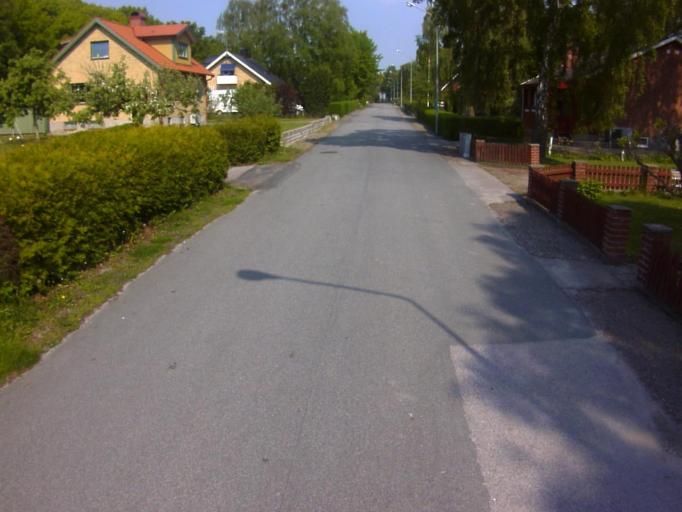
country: SE
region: Blekinge
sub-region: Solvesborgs Kommun
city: Soelvesborg
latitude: 56.0089
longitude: 14.7289
